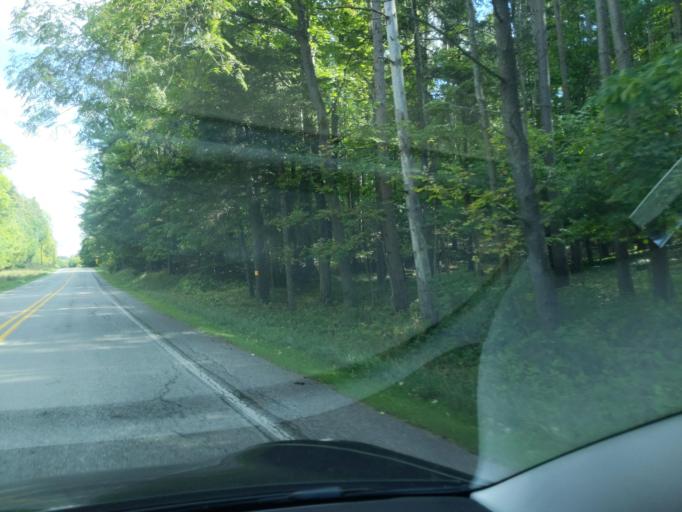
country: US
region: Michigan
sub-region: Antrim County
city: Bellaire
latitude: 45.0490
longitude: -85.3110
